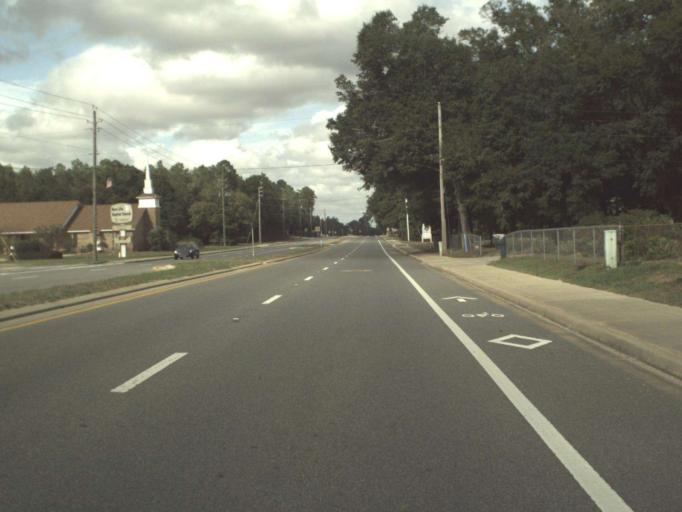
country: US
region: Florida
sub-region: Santa Rosa County
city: Point Baker
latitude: 30.6856
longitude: -87.0538
